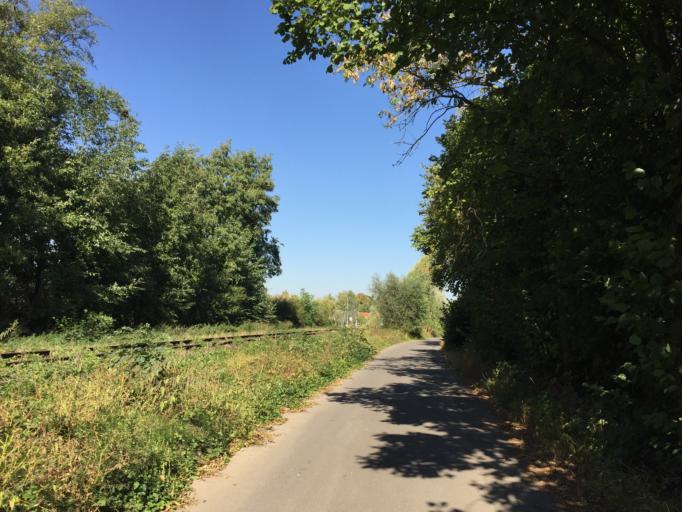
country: DE
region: Hesse
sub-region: Regierungsbezirk Giessen
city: Hungen
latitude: 50.4481
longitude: 8.9129
